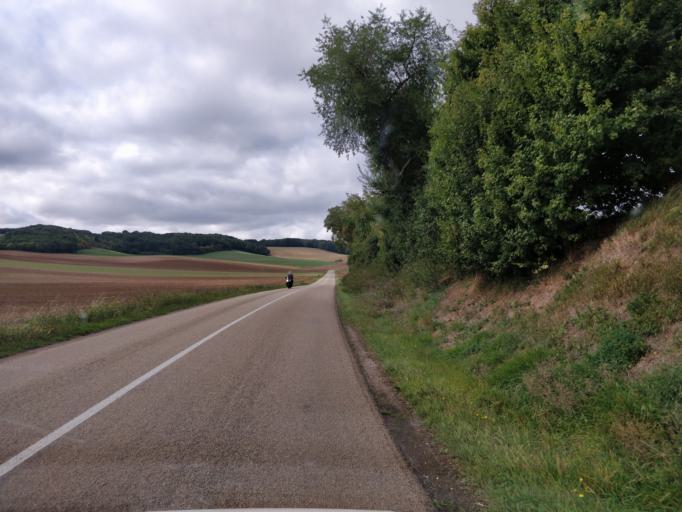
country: FR
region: Bourgogne
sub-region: Departement de l'Yonne
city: Saint-Florentin
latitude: 48.0865
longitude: 3.6959
